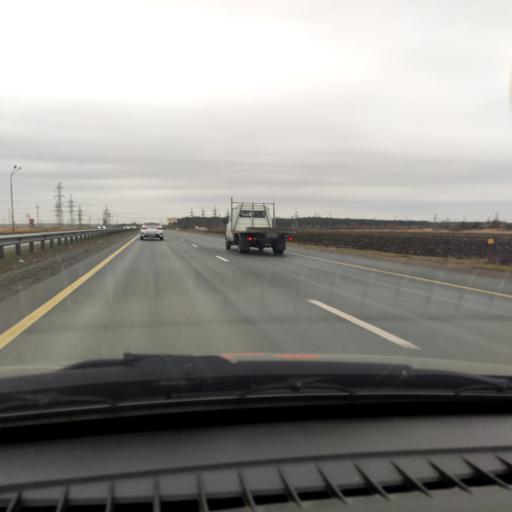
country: RU
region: Samara
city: Zhigulevsk
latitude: 53.5486
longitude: 49.5091
